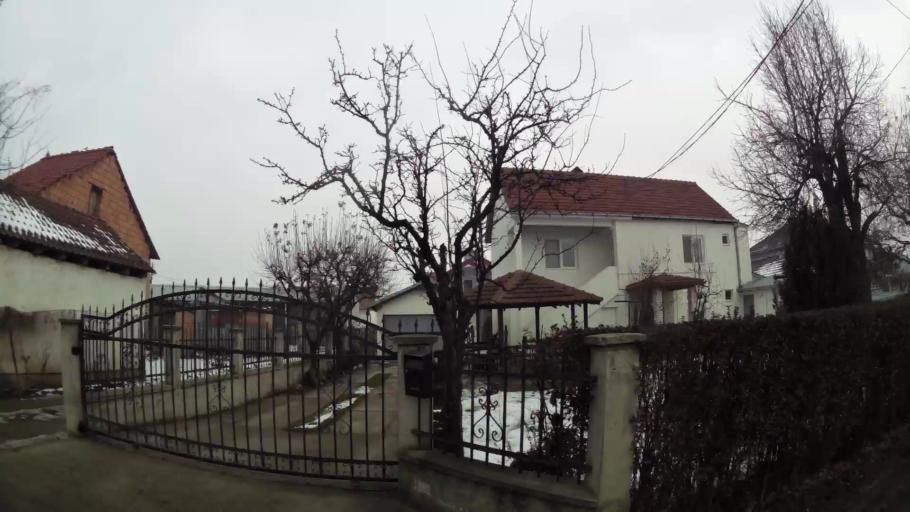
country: MK
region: Ilinden
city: Idrizovo
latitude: 41.9630
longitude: 21.5672
